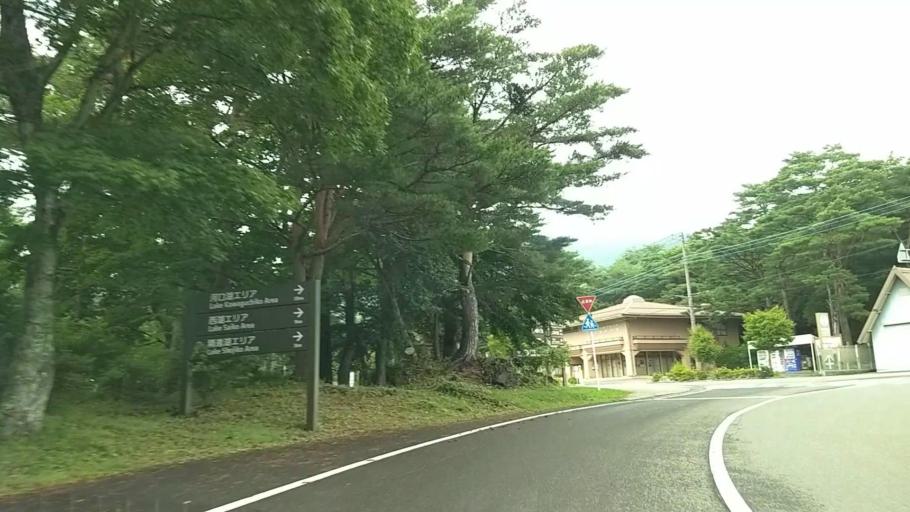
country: JP
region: Yamanashi
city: Fujikawaguchiko
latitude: 35.4644
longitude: 138.6024
